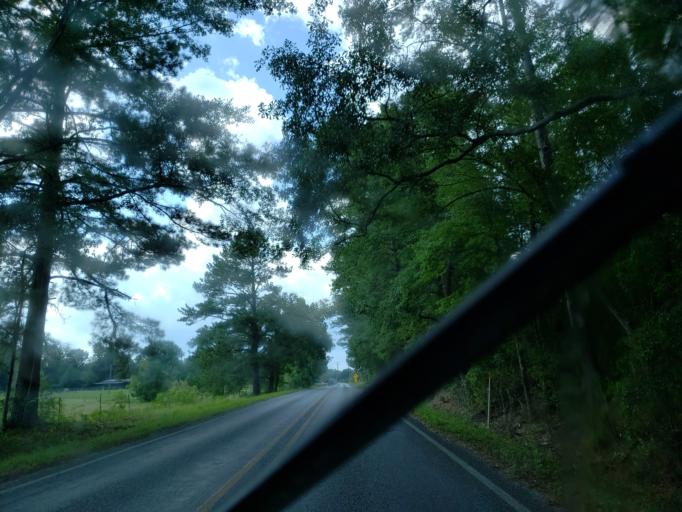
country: US
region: Mississippi
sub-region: Jones County
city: Sharon
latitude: 31.9161
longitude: -89.0192
